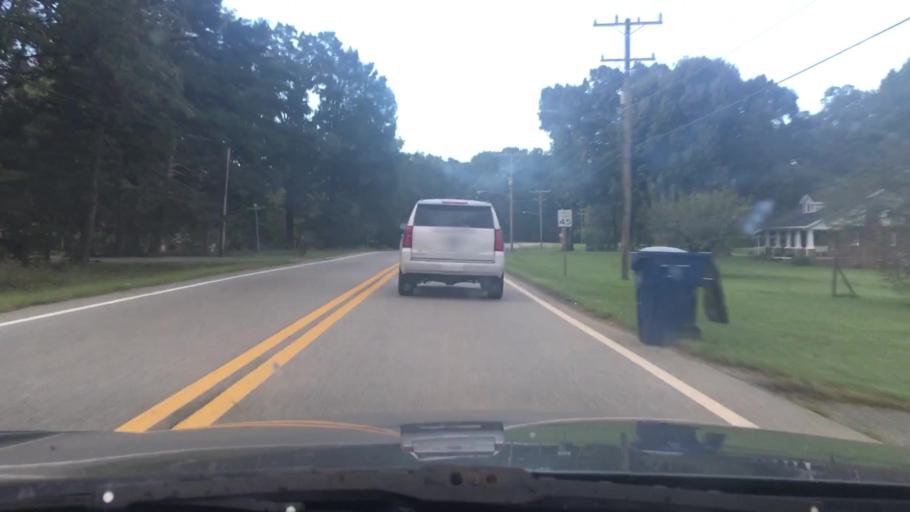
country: US
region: North Carolina
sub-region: Alamance County
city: Green Level
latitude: 36.1325
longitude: -79.3449
